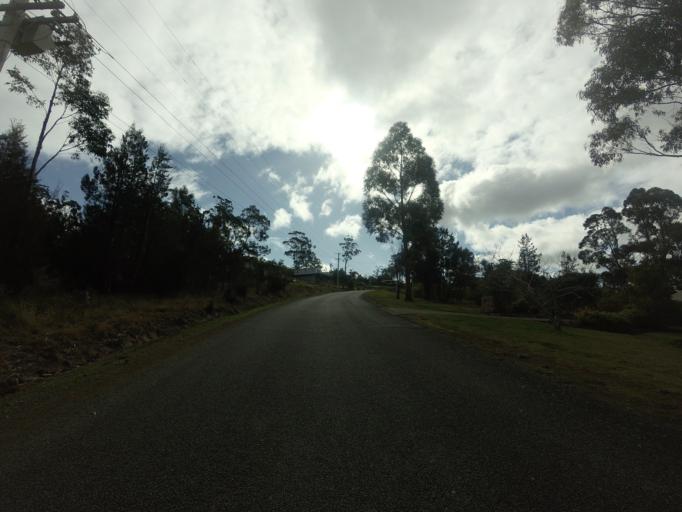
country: AU
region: Tasmania
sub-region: Sorell
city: Sorell
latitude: -42.5417
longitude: 147.9104
